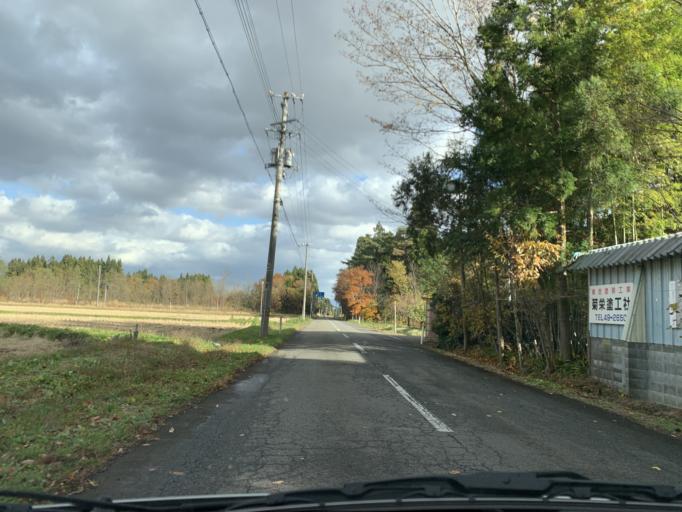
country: JP
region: Iwate
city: Mizusawa
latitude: 39.1164
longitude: 140.9972
